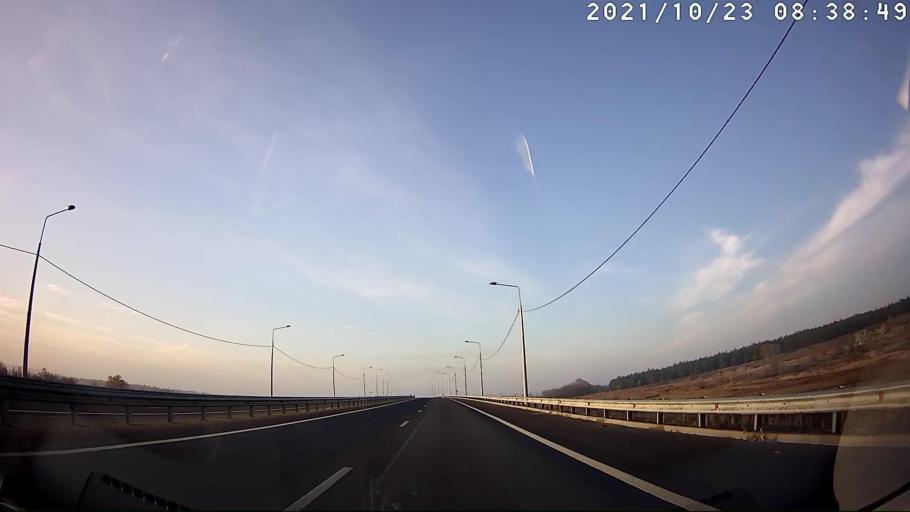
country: RU
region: Saratov
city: Sinodskoye
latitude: 52.0131
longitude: 46.6917
